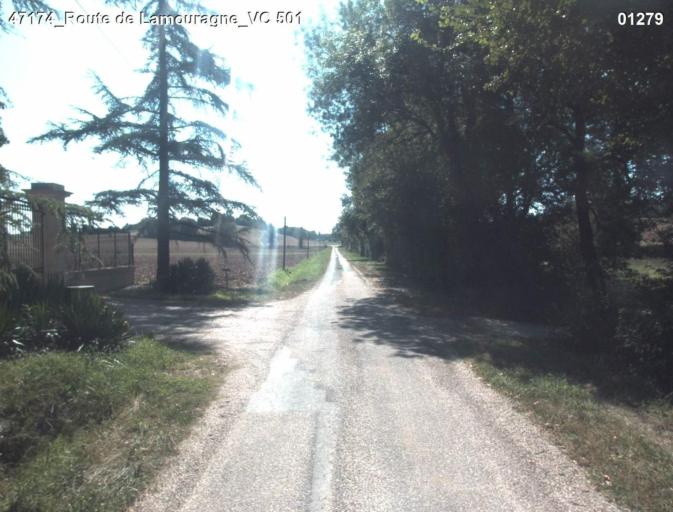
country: FR
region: Midi-Pyrenees
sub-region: Departement du Gers
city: Condom
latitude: 44.0370
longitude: 0.3899
